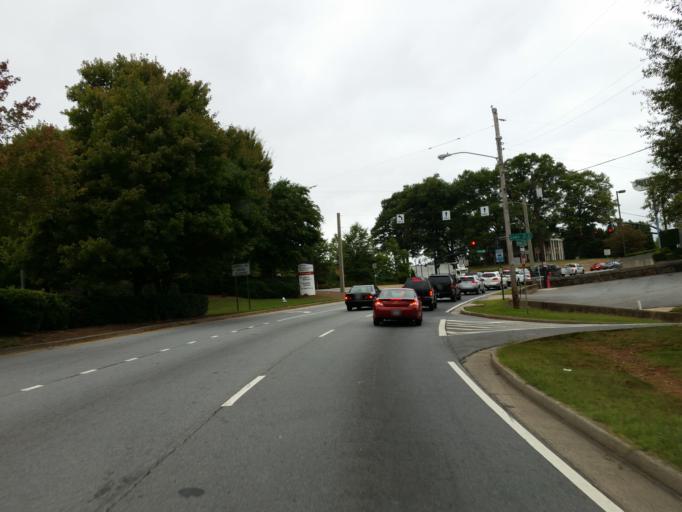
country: US
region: Georgia
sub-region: Cobb County
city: Marietta
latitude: 33.9694
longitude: -84.5497
